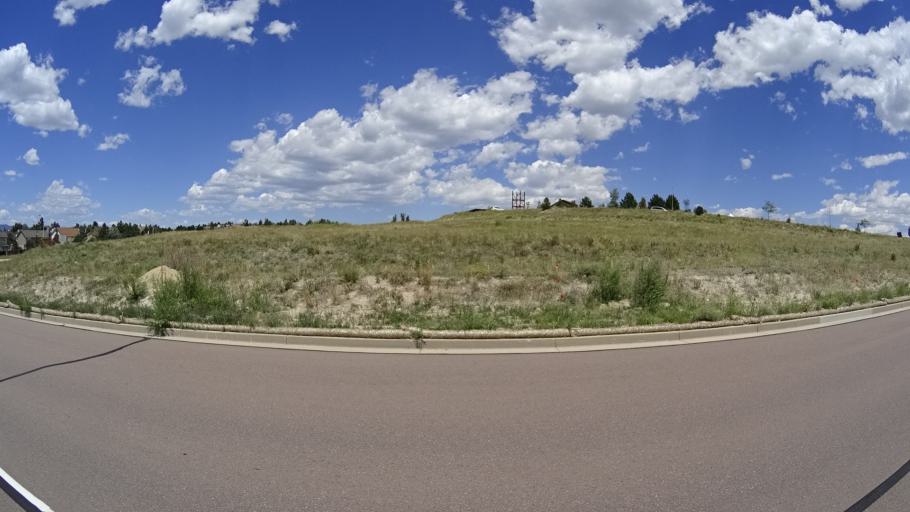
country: US
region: Colorado
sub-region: El Paso County
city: Black Forest
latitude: 38.9547
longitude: -104.7381
